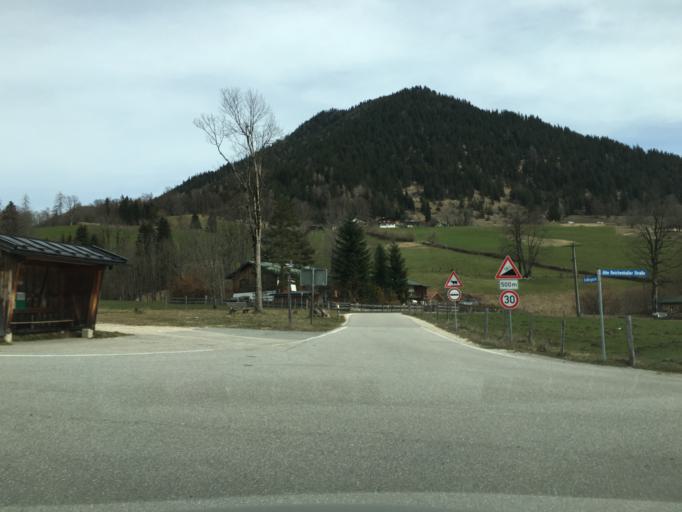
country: DE
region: Bavaria
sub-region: Upper Bavaria
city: Ramsau
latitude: 47.6156
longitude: 12.8759
